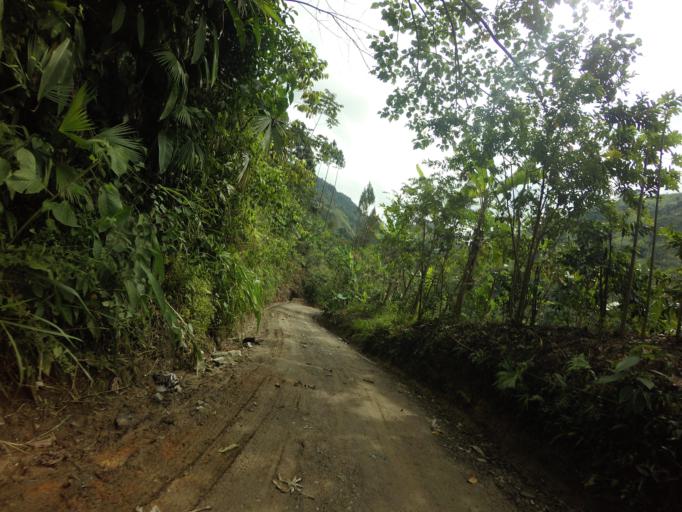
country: CO
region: Caldas
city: Marquetalia
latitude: 5.3281
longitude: -75.0482
